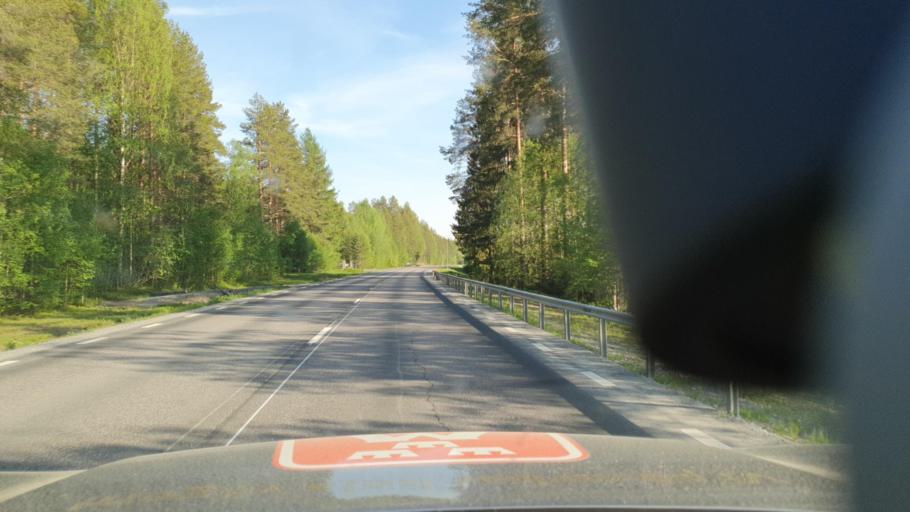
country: SE
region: Norrbotten
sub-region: Bodens Kommun
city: Boden
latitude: 65.8765
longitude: 21.4083
